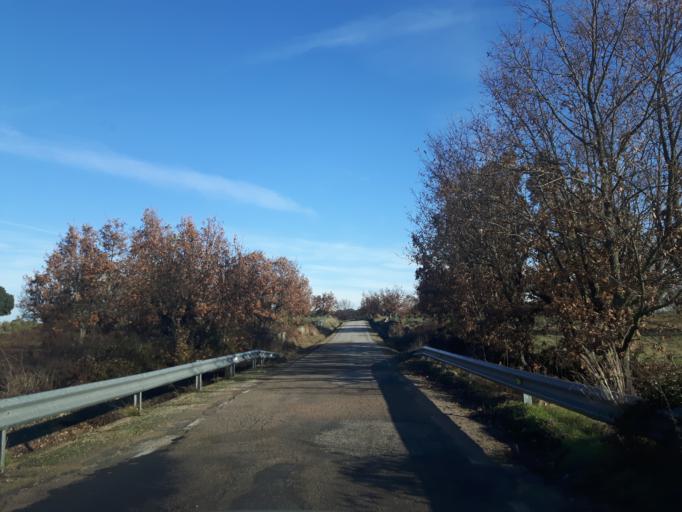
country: ES
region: Castille and Leon
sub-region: Provincia de Salamanca
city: Cerralbo
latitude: 40.9391
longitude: -6.6198
